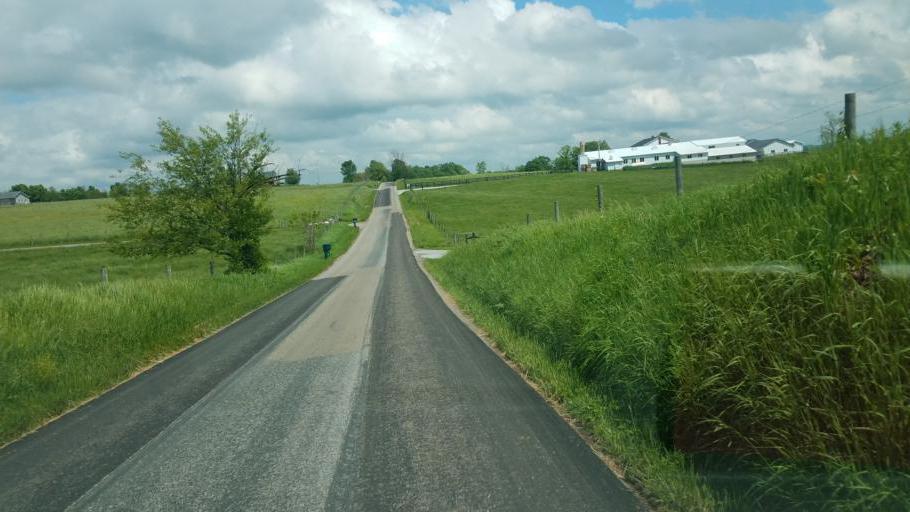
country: US
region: Ohio
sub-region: Wayne County
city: Apple Creek
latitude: 40.6752
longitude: -81.7526
